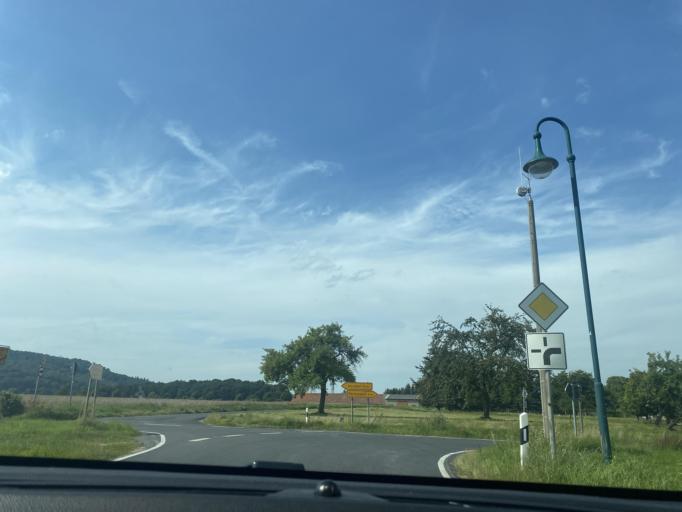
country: DE
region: Saxony
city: Sohland am Rotstein
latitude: 51.0978
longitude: 14.7898
